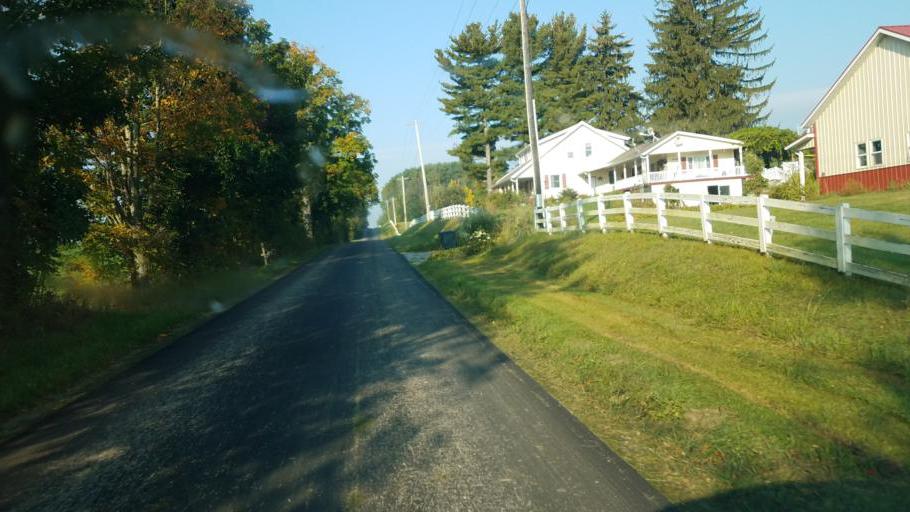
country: US
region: Ohio
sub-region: Knox County
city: Fredericktown
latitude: 40.5225
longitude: -82.6392
